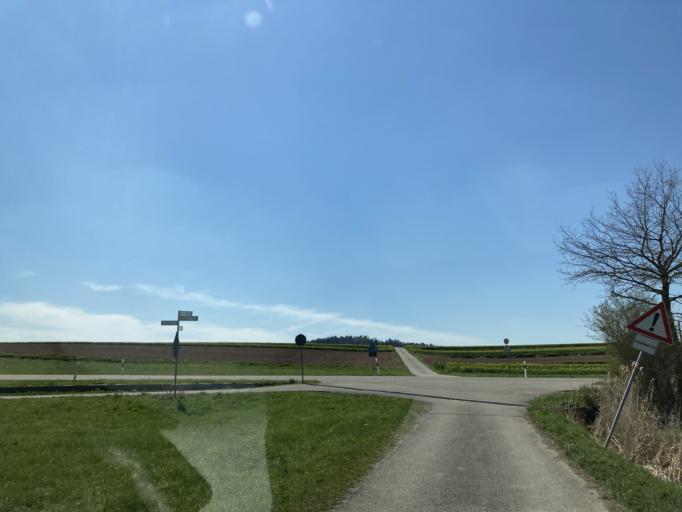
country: DE
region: Baden-Wuerttemberg
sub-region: Tuebingen Region
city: Rottenburg
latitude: 48.5129
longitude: 8.9247
